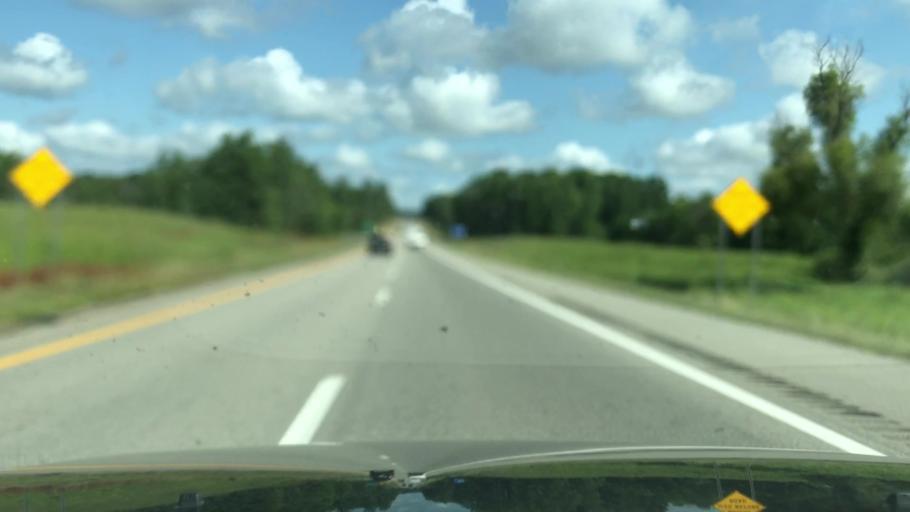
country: US
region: Michigan
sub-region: Montcalm County
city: Howard City
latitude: 43.4704
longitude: -85.4766
